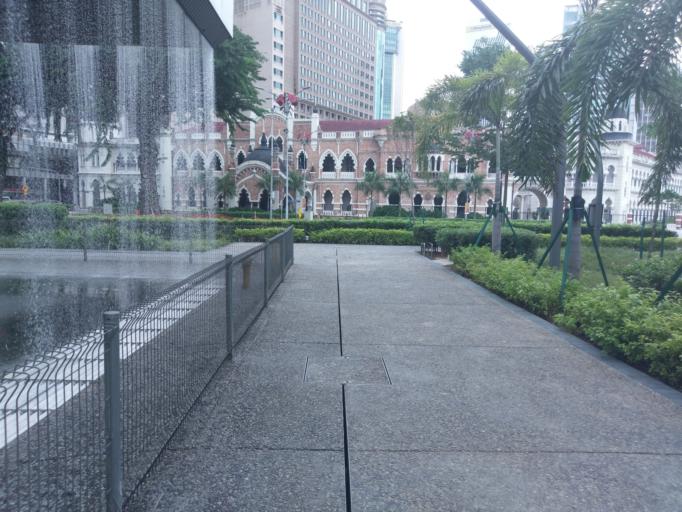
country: MY
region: Kuala Lumpur
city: Kuala Lumpur
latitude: 3.1506
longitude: 101.6943
